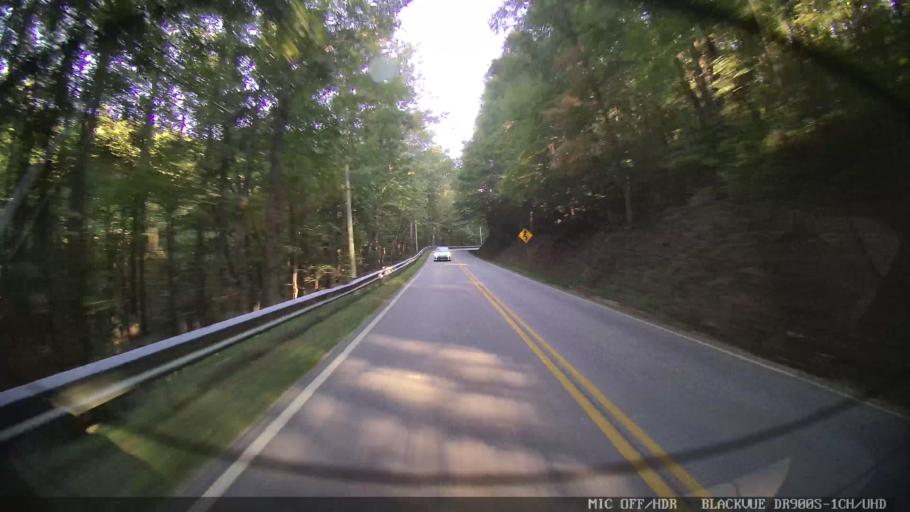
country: US
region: Georgia
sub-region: Lumpkin County
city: Dahlonega
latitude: 34.7004
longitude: -84.0294
